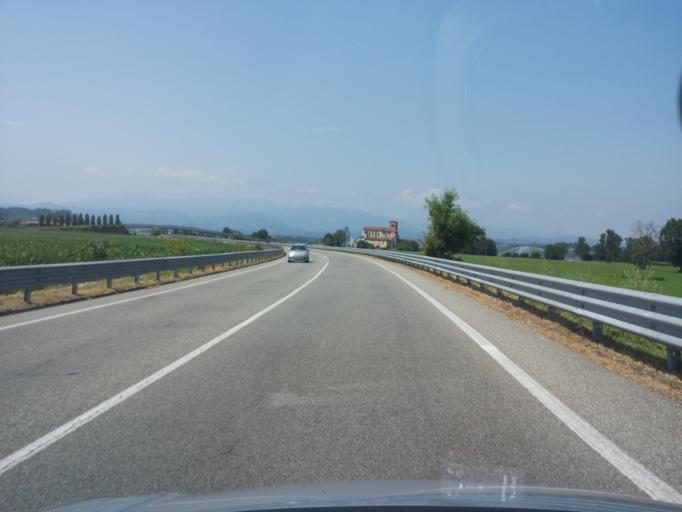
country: IT
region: Piedmont
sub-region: Provincia di Biella
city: Mottalciata
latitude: 45.5141
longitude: 8.2117
